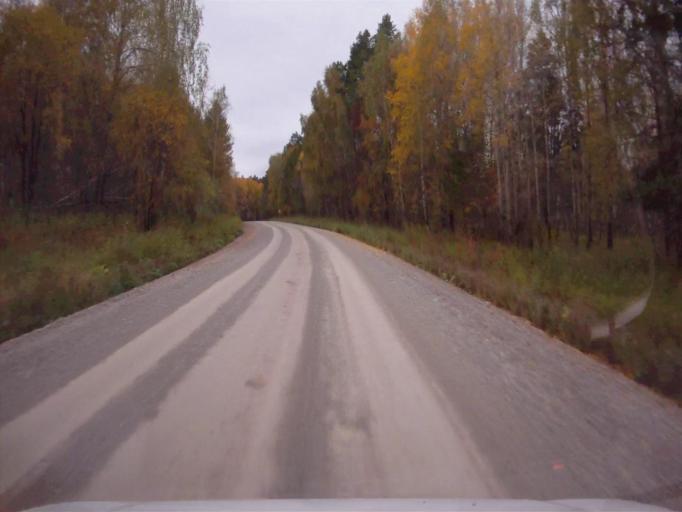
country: RU
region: Chelyabinsk
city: Nyazepetrovsk
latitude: 56.0662
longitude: 59.4386
